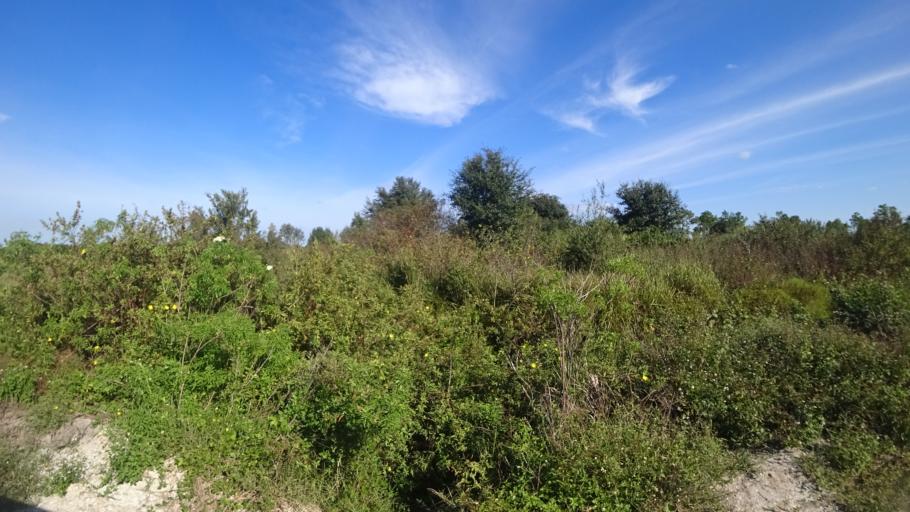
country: US
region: Florida
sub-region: Sarasota County
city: The Meadows
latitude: 27.4452
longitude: -82.3374
